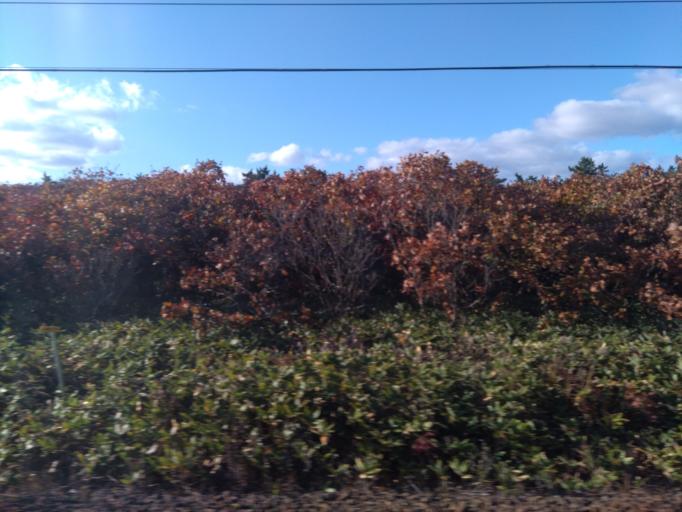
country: JP
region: Hokkaido
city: Niseko Town
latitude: 42.5527
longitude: 140.4204
